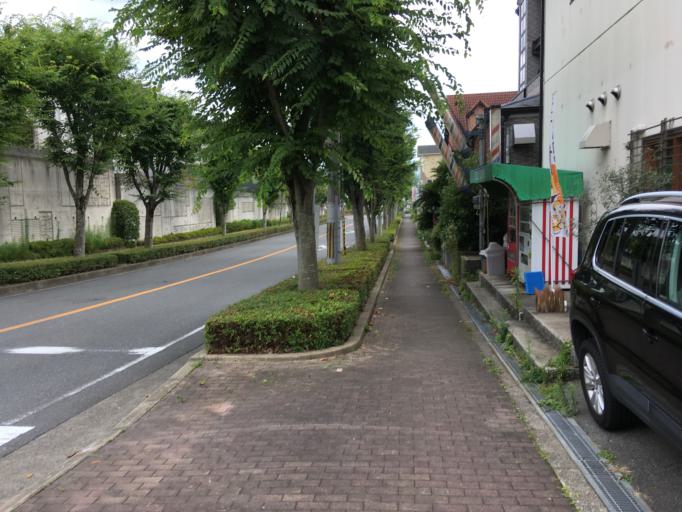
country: JP
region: Nara
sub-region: Ikoma-shi
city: Ikoma
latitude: 34.6760
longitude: 135.7188
